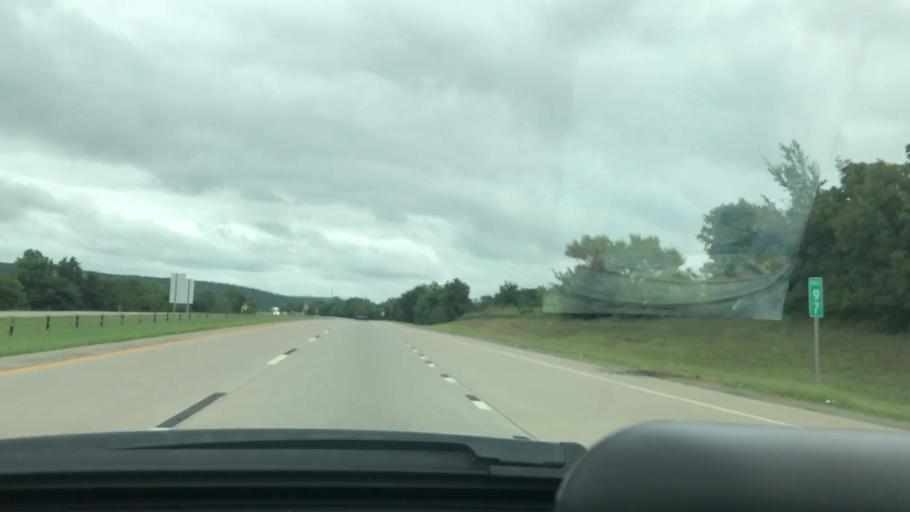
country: US
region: Oklahoma
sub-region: Pittsburg County
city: Krebs
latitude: 35.0042
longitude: -95.7192
